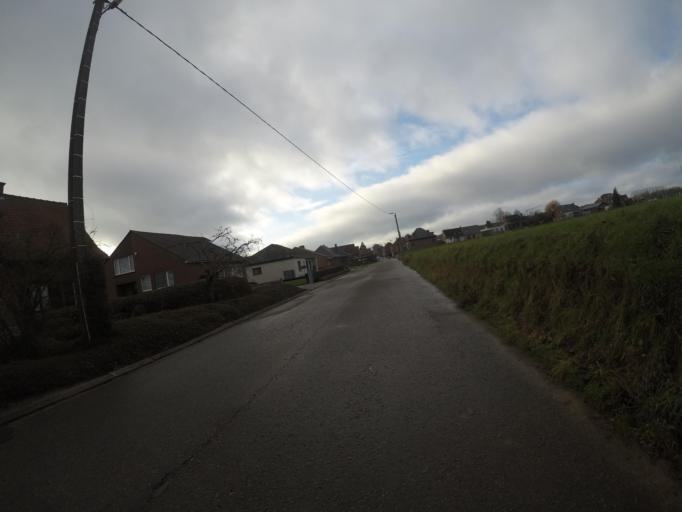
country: BE
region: Flanders
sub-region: Provincie Vlaams-Brabant
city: Gooik
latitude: 50.7787
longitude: 4.1270
